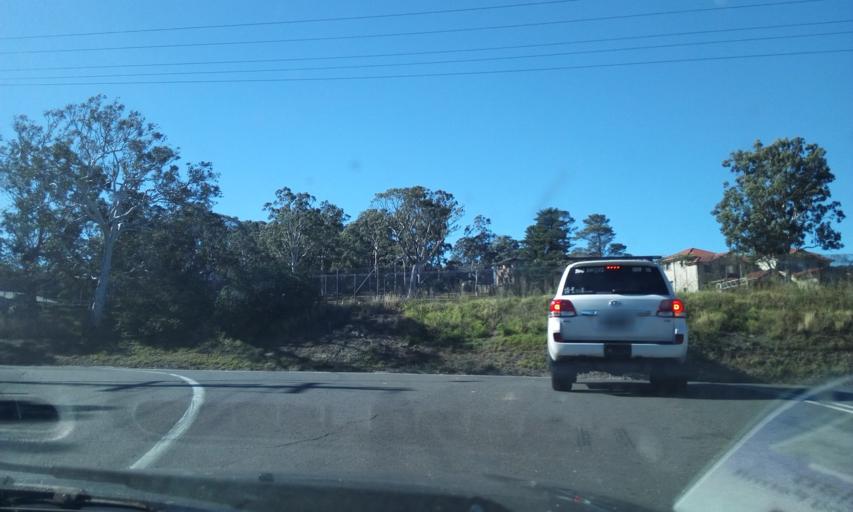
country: AU
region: New South Wales
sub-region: Wollongong
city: Dapto
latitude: -34.5168
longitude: 150.7833
